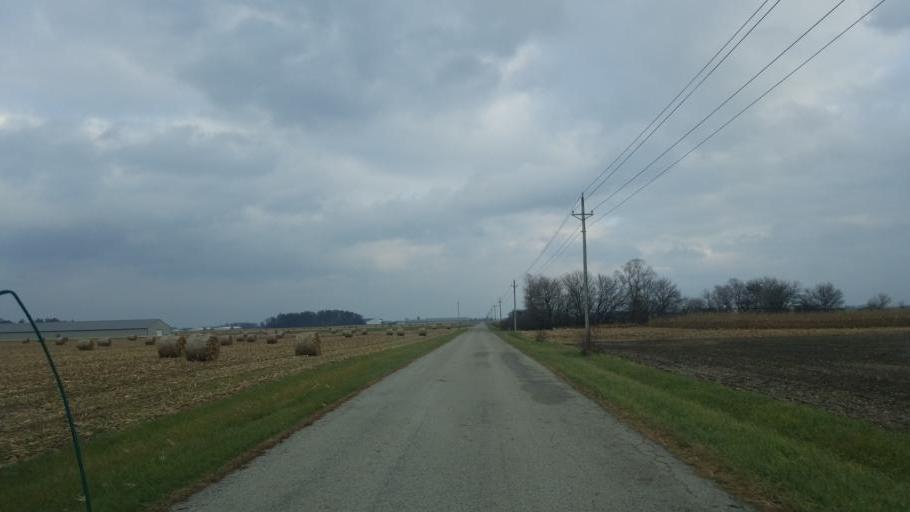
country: US
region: Indiana
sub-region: Adams County
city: Geneva
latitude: 40.5132
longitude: -84.8724
